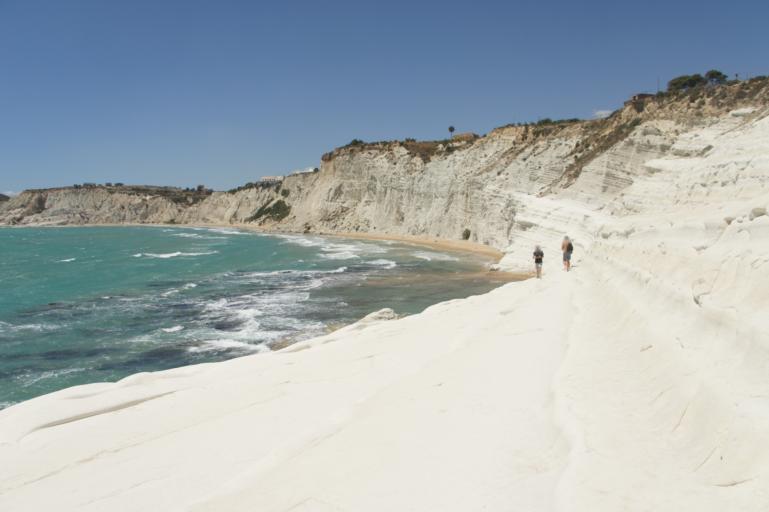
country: IT
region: Sicily
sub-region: Agrigento
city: Realmonte
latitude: 37.2899
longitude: 13.4731
